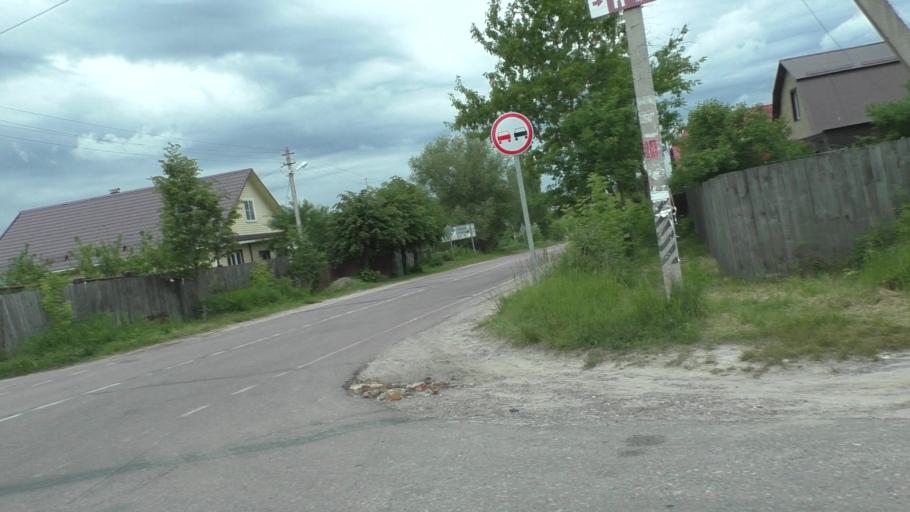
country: RU
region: Moskovskaya
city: Il'inskiy Pogost
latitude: 55.4727
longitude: 38.8941
